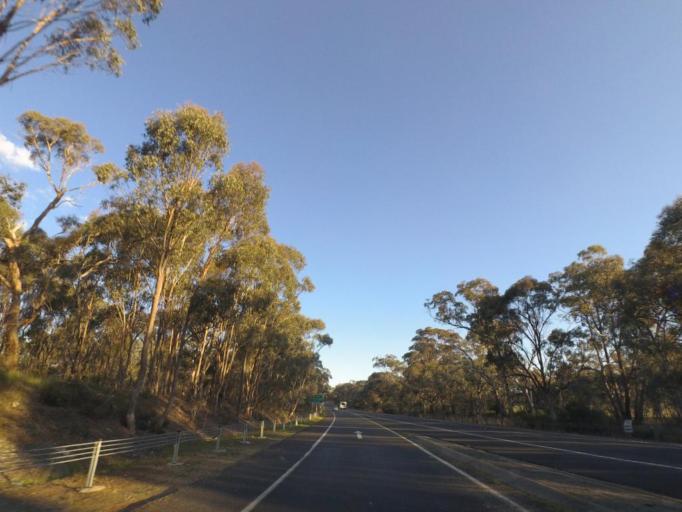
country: AU
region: Victoria
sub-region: Murrindindi
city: Kinglake West
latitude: -37.0675
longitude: 145.1018
